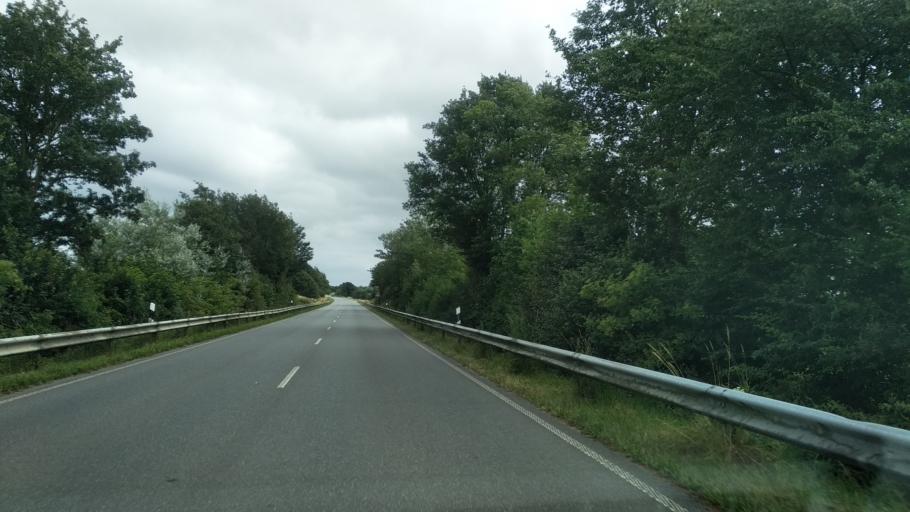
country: DE
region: Schleswig-Holstein
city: Neuberend
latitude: 54.5429
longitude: 9.5486
